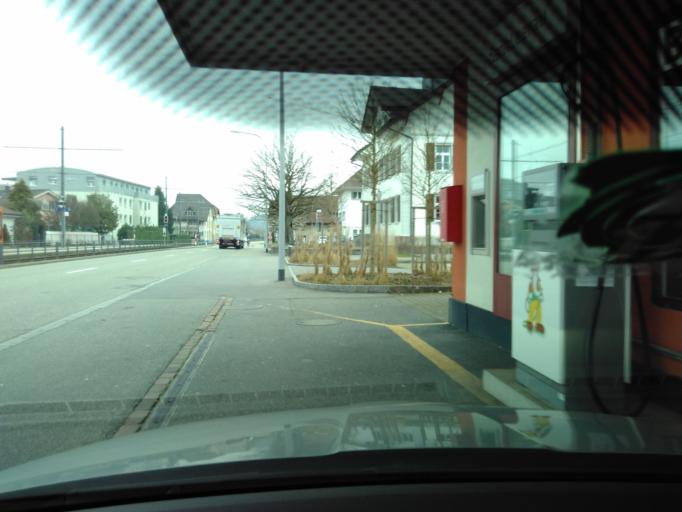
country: CH
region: Aargau
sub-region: Bezirk Kulm
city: Schoftland
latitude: 47.3197
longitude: 8.0530
